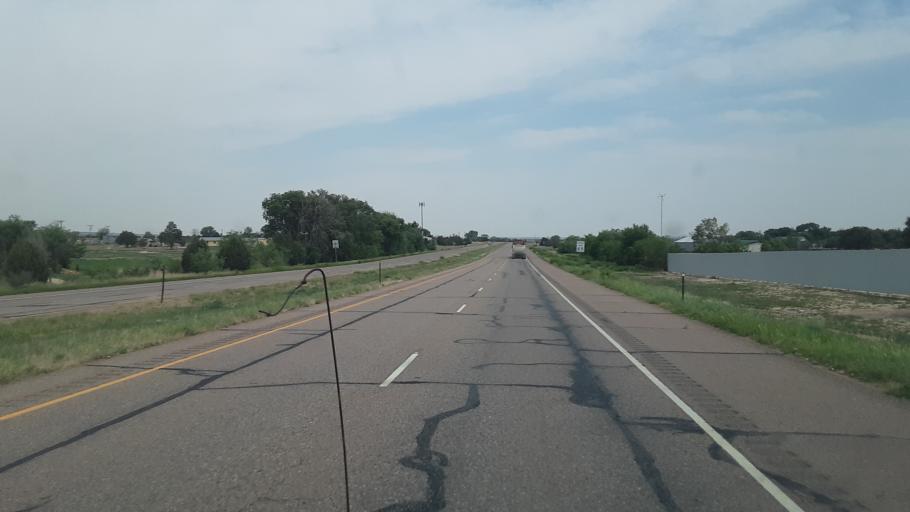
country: US
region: Colorado
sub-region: Fremont County
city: Penrose
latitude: 38.4061
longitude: -104.9949
